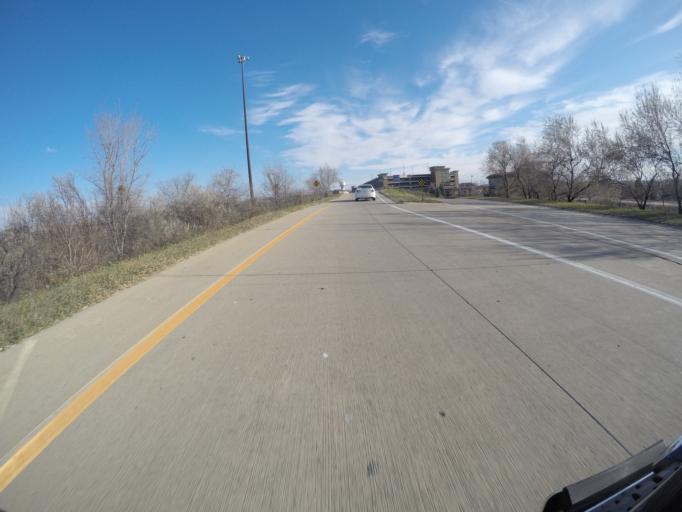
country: US
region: Minnesota
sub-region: Hennepin County
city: Eden Prairie
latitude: 44.8607
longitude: -93.4459
